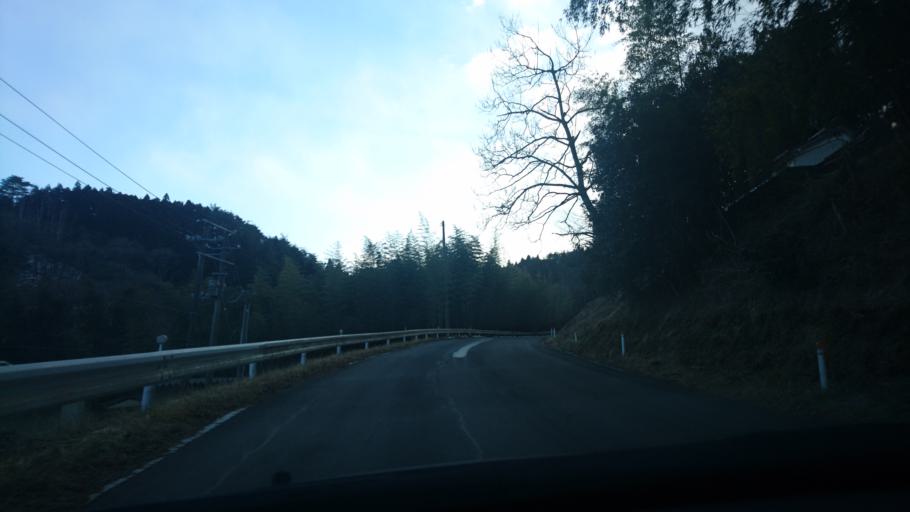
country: JP
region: Iwate
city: Ofunato
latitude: 38.9115
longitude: 141.5308
